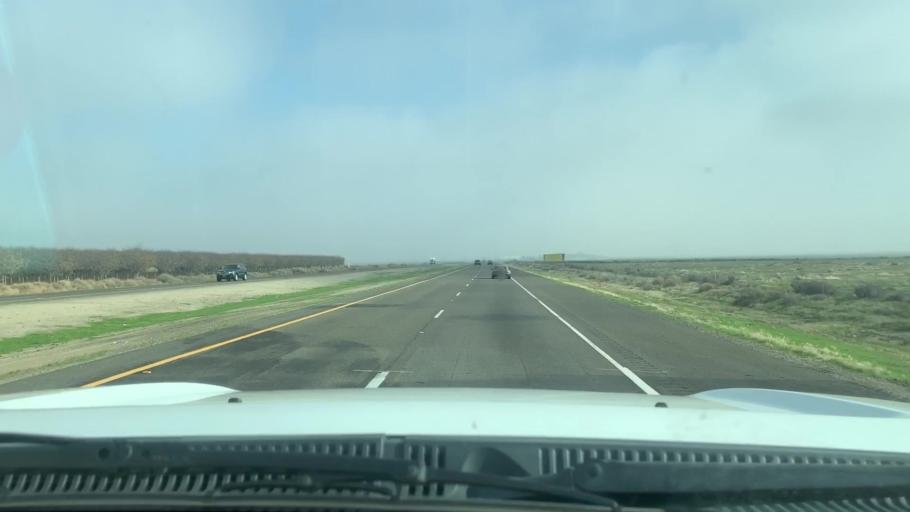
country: US
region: California
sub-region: Kern County
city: Lost Hills
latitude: 35.6147
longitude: -119.8884
